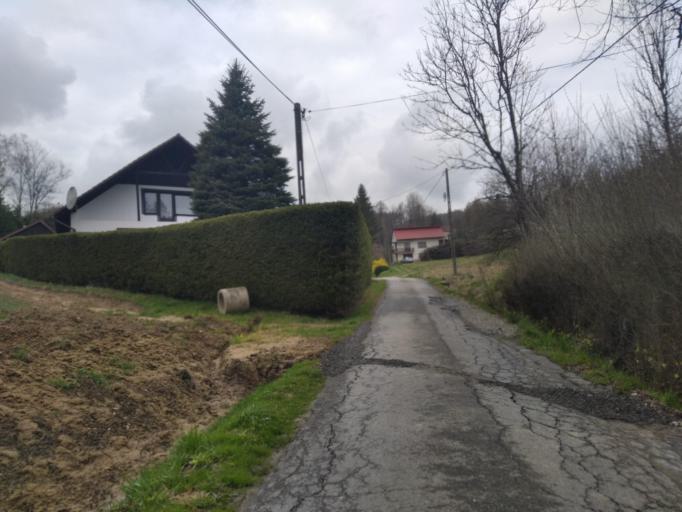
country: PL
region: Subcarpathian Voivodeship
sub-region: Powiat strzyzowski
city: Wisniowa
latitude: 49.8791
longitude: 21.7054
